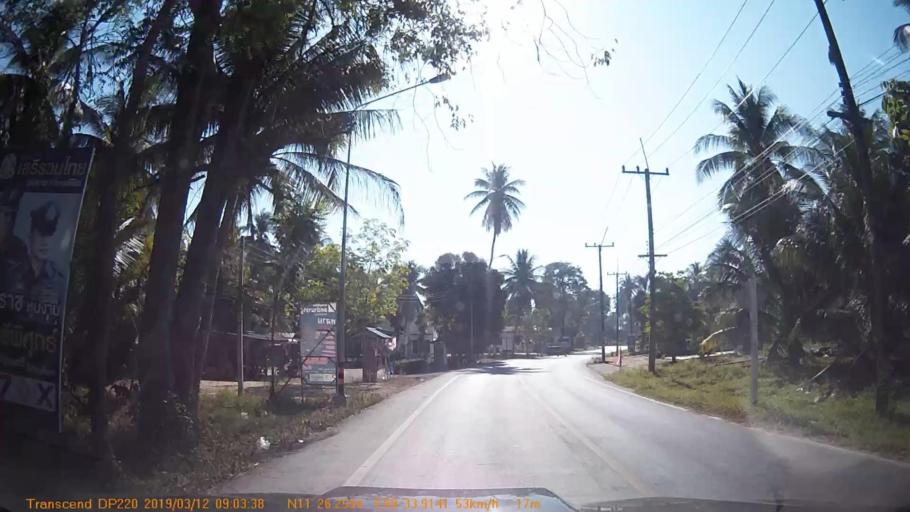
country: TH
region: Prachuap Khiri Khan
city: Thap Sakae
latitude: 11.4376
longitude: 99.5654
